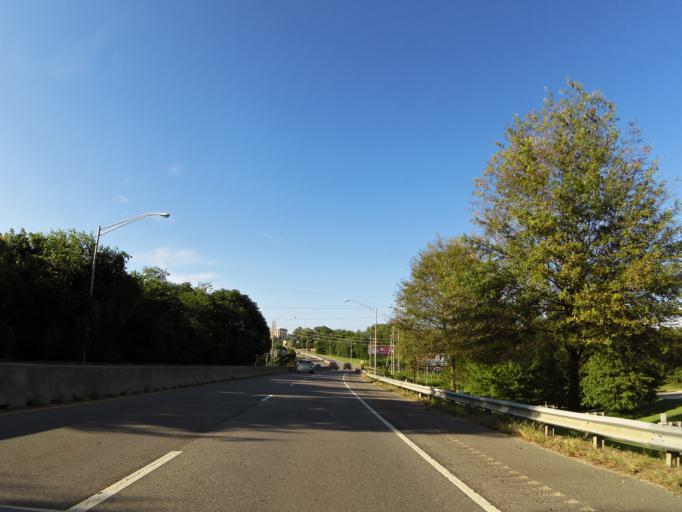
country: US
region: Alabama
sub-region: Lauderdale County
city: Florence
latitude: 34.7906
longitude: -87.6733
